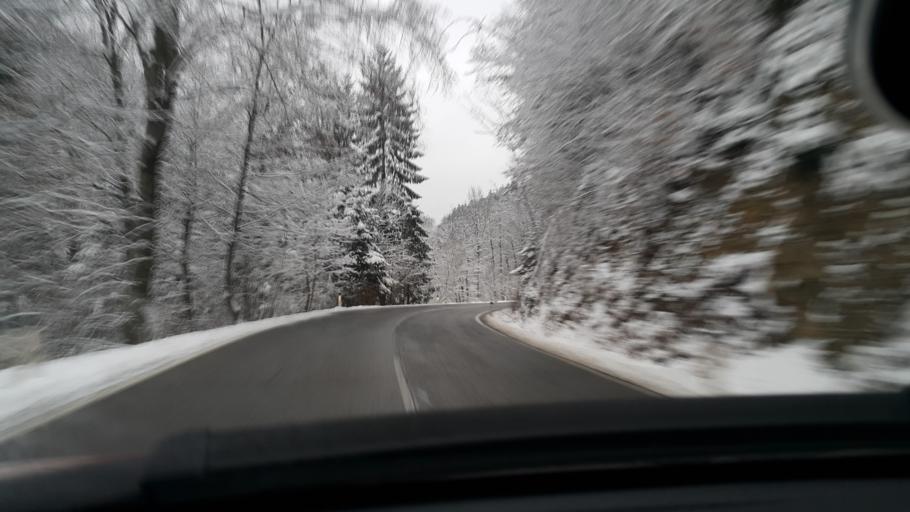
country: AT
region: Styria
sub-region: Politischer Bezirk Graz-Umgebung
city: Sankt Oswald bei Plankenwarth
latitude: 47.0834
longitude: 15.2541
